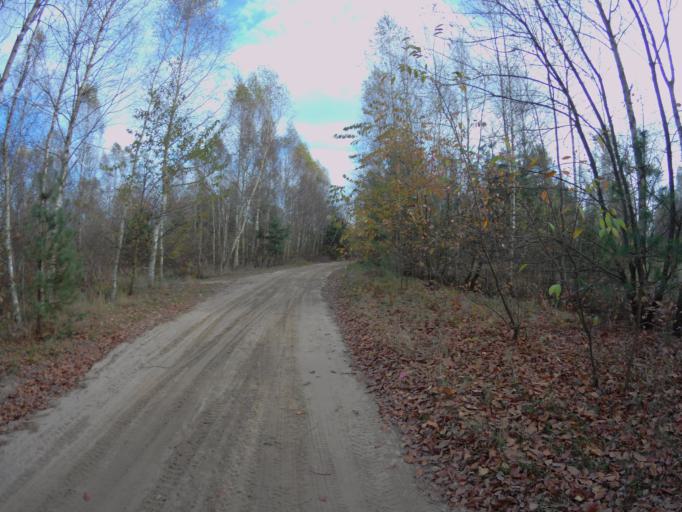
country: PL
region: Subcarpathian Voivodeship
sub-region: Powiat kolbuszowski
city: Lipnica
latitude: 50.3252
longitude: 21.9387
